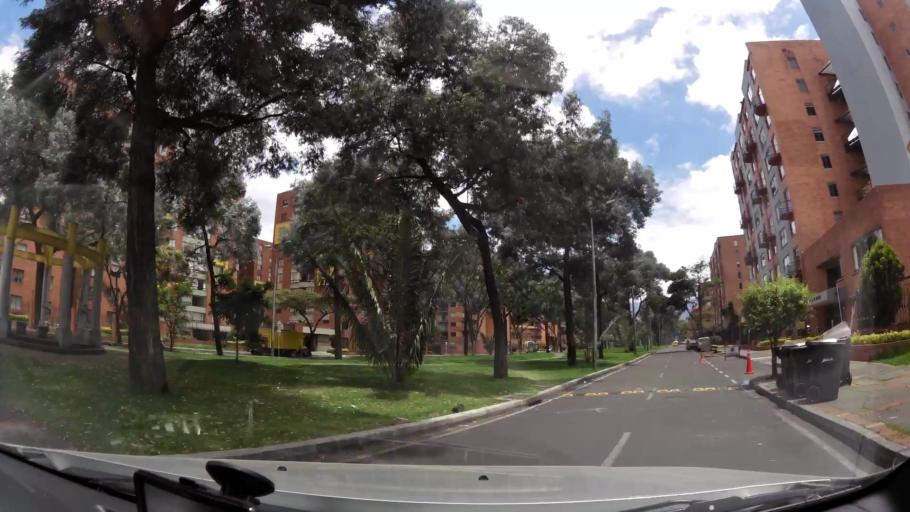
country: CO
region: Bogota D.C.
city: Bogota
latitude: 4.6431
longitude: -74.1038
